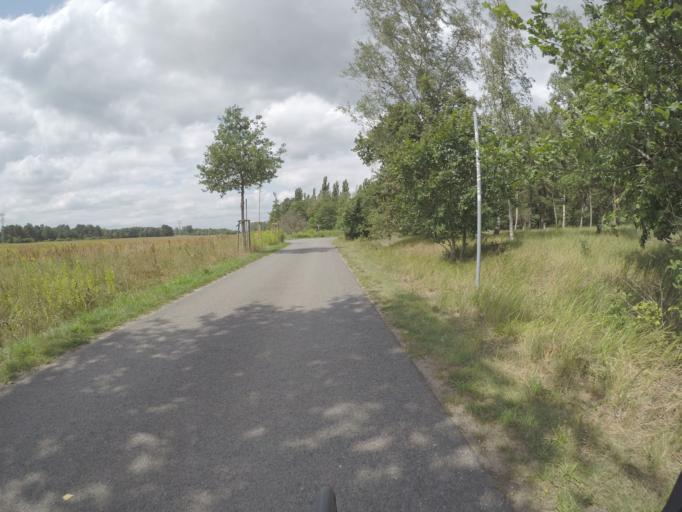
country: DE
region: Brandenburg
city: Falkensee
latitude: 52.6051
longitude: 13.0841
